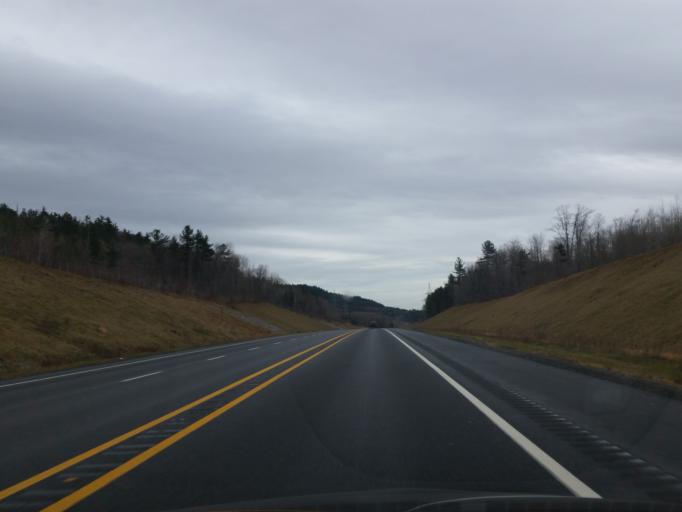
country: CA
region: Quebec
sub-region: Outaouais
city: Papineauville
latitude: 45.6661
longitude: -74.8952
